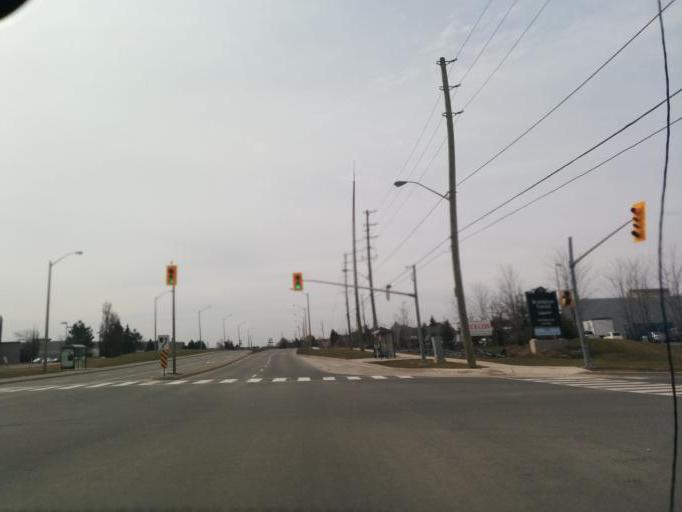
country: CA
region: Ontario
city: Brampton
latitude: 43.7147
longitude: -79.8066
